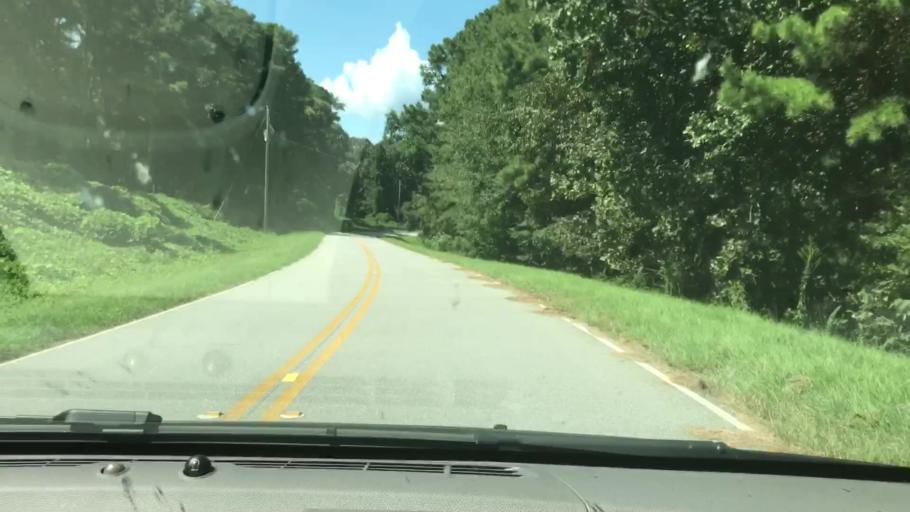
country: US
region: Georgia
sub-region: Troup County
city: La Grange
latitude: 33.0750
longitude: -85.1296
